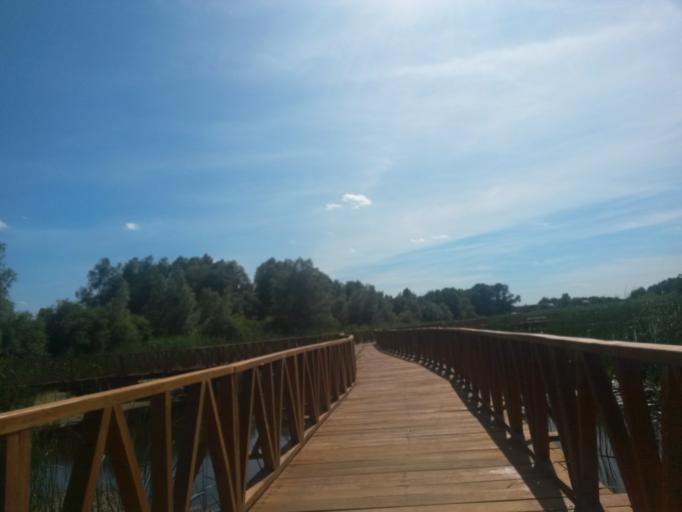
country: HR
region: Osjecko-Baranjska
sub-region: Grad Osijek
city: Bilje
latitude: 45.6088
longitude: 18.7954
